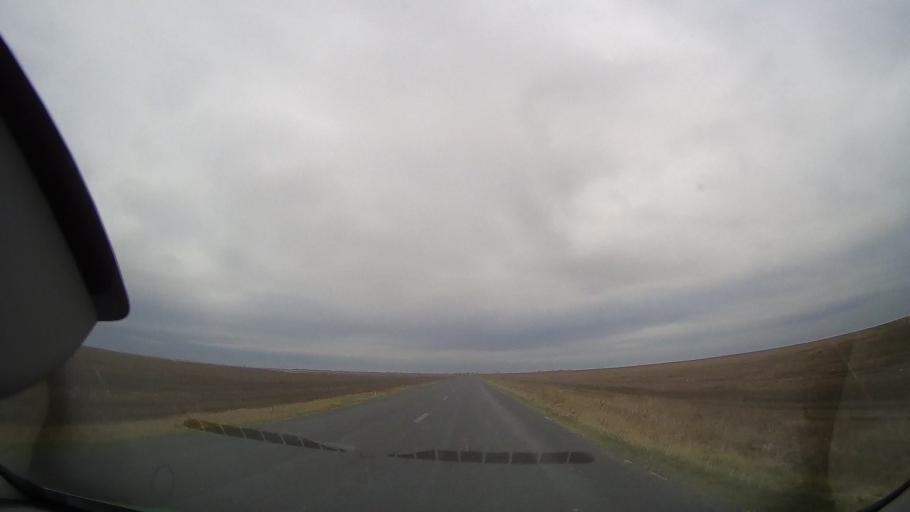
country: RO
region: Buzau
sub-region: Comuna Padina
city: Padina
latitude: 44.8091
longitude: 27.1283
